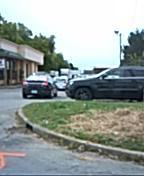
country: US
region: Kentucky
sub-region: Jefferson County
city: Hurstbourne
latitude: 38.2463
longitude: -85.5758
